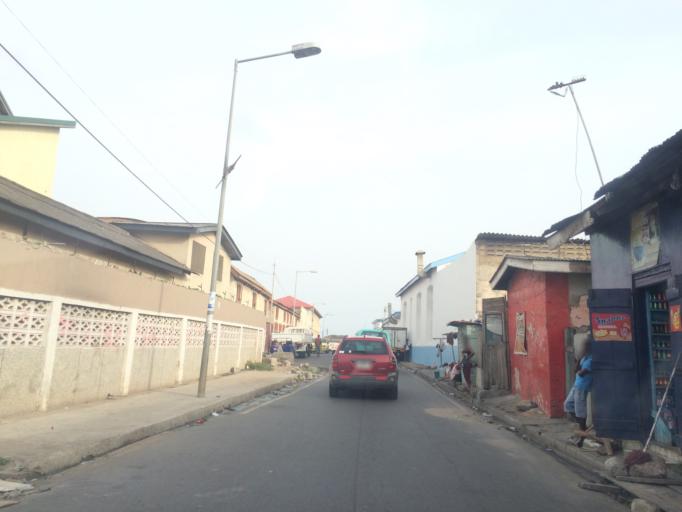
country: GH
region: Greater Accra
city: Accra
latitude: 5.5361
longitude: -0.2119
